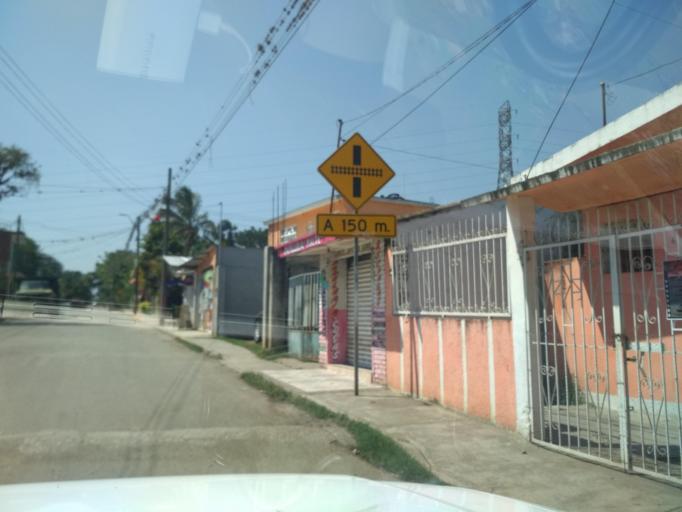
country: MX
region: Veracruz
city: Amatlan de los Reyes
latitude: 18.8533
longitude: -96.9194
